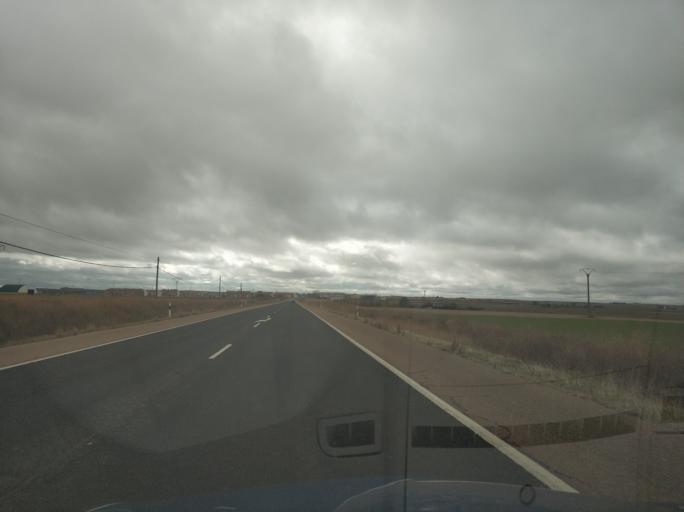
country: ES
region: Castille and Leon
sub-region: Provincia de Salamanca
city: Castellanos de Moriscos
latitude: 41.0285
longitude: -5.5828
